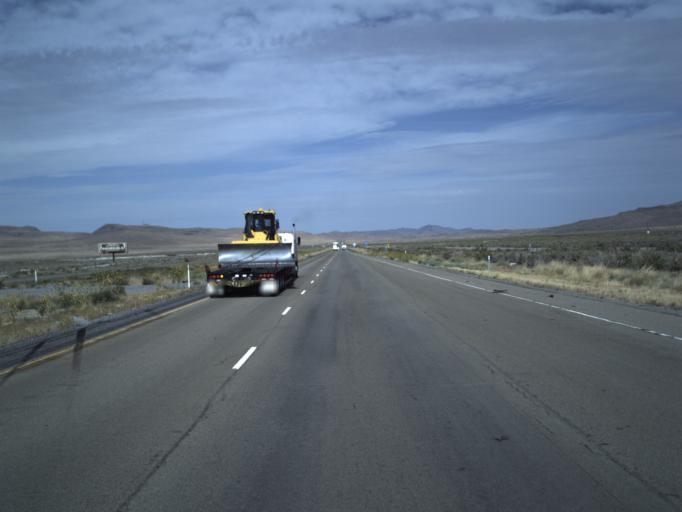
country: US
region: Utah
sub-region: Tooele County
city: Grantsville
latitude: 40.7664
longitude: -112.7876
